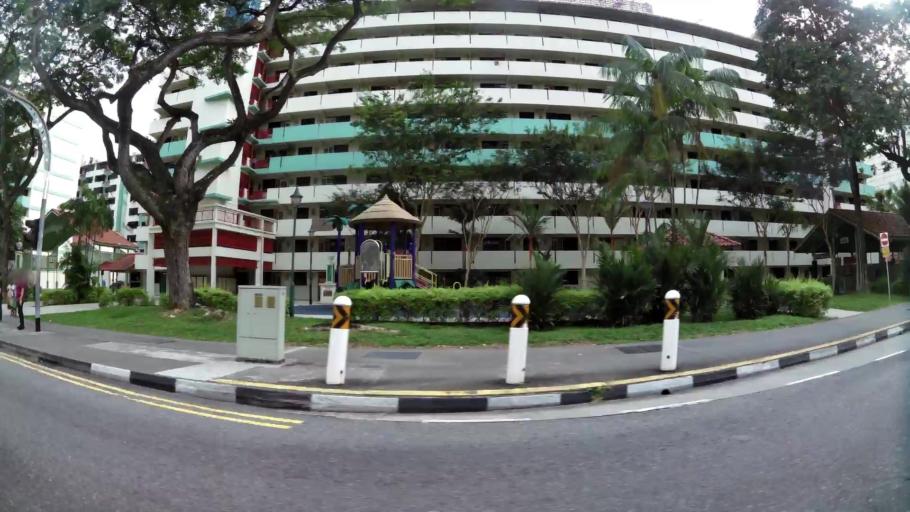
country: SG
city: Singapore
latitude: 1.3408
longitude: 103.8482
